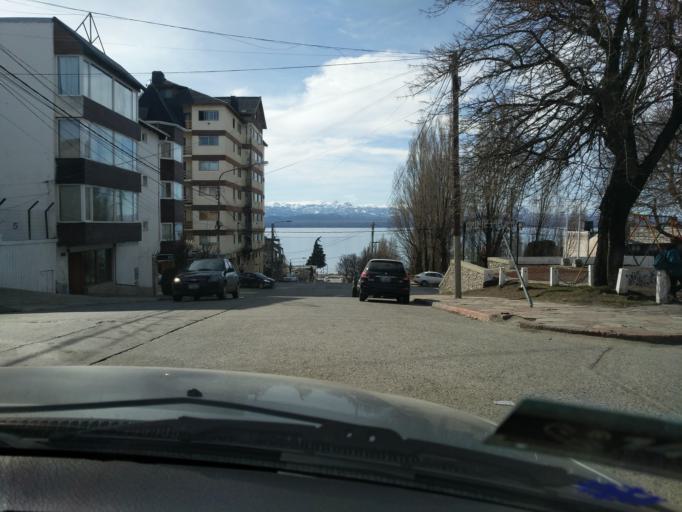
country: AR
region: Rio Negro
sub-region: Departamento de Bariloche
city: San Carlos de Bariloche
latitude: -41.1357
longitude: -71.2942
